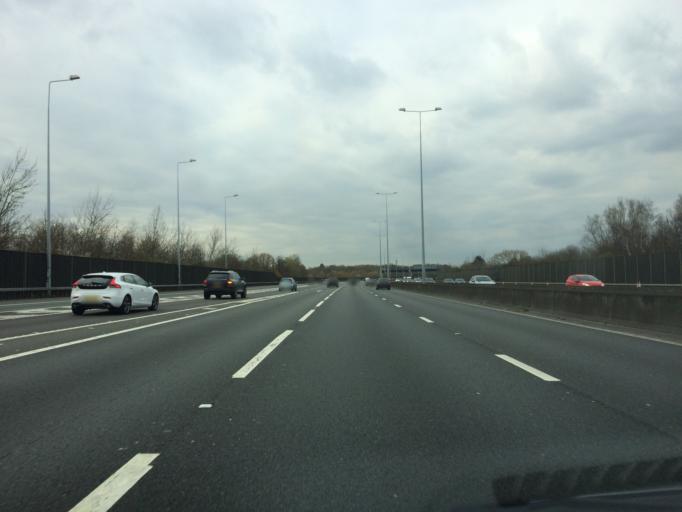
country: GB
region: England
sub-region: Surrey
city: Virginia Water
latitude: 51.4056
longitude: -0.5400
